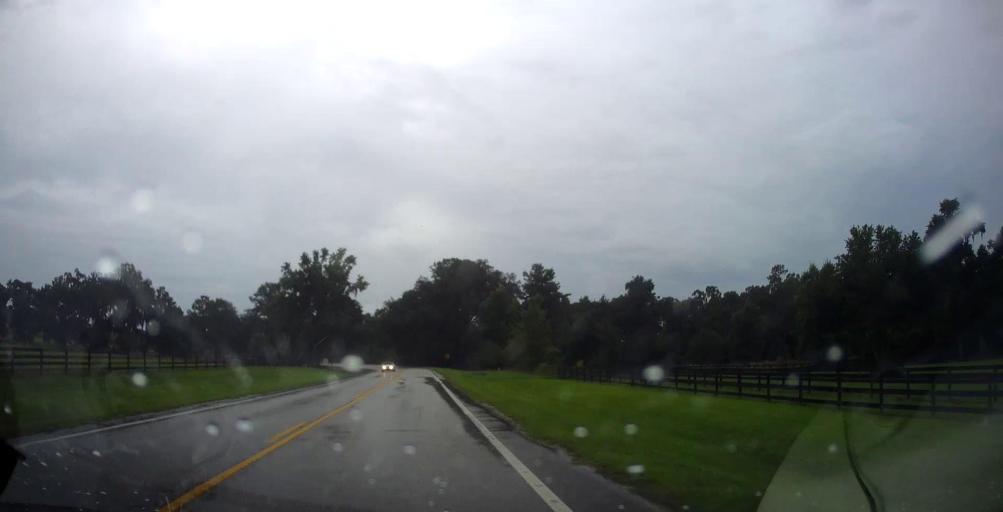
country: US
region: Florida
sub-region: Marion County
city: Citra
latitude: 29.3758
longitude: -82.2516
